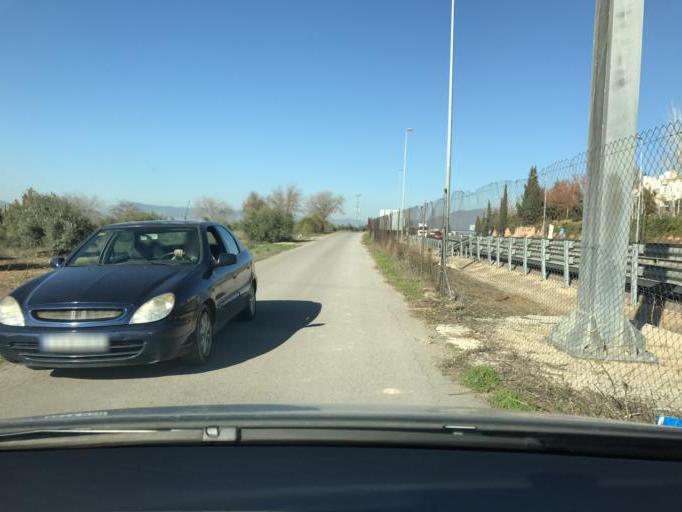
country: ES
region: Andalusia
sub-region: Provincia de Granada
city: Albolote
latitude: 37.2518
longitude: -3.6578
